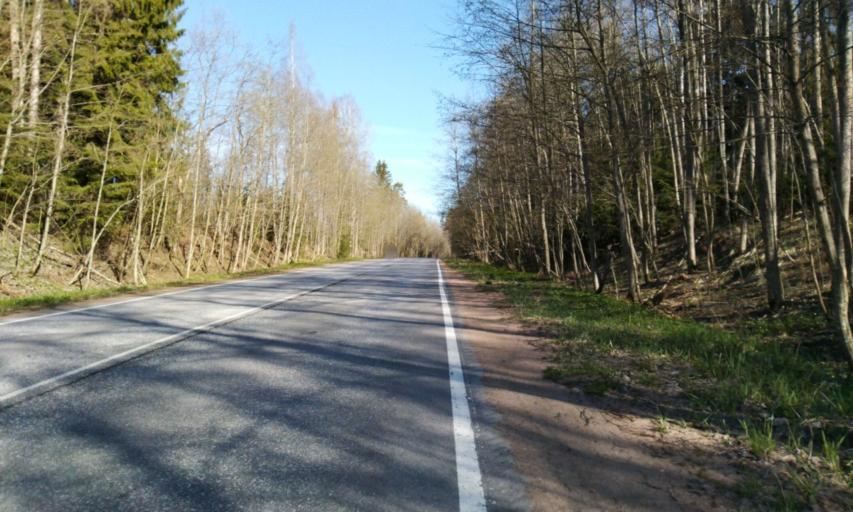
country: RU
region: Leningrad
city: Garbolovo
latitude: 60.3622
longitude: 30.4439
